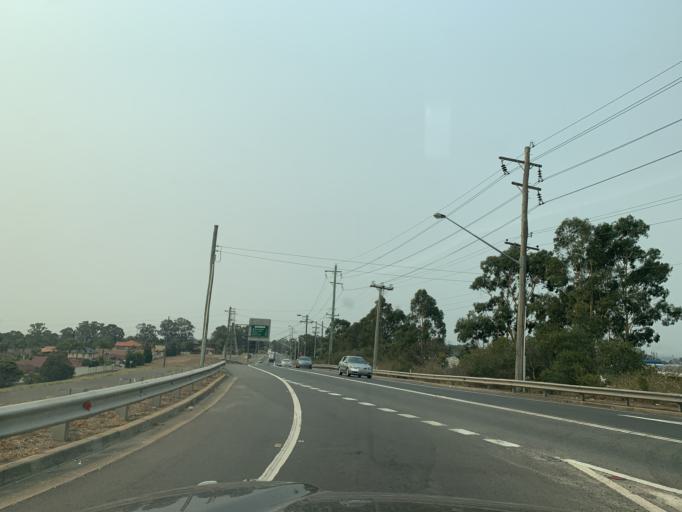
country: AU
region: New South Wales
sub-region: Holroyd
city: Girraween
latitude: -33.8017
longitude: 150.9161
